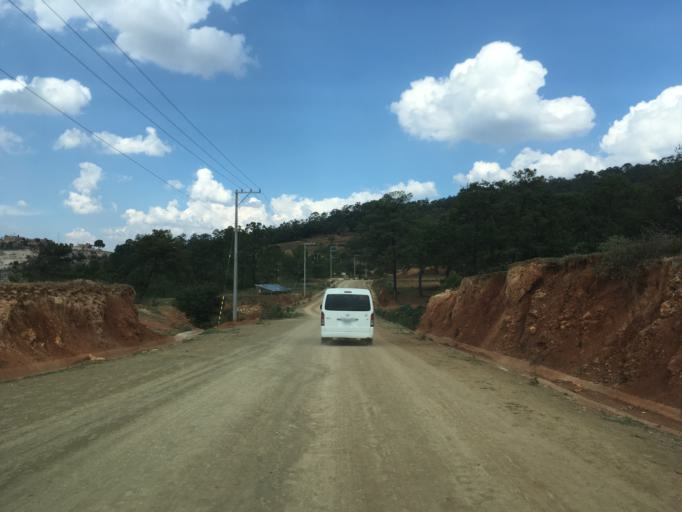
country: MX
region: Oaxaca
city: Santiago Tilantongo
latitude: 17.2179
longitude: -97.2752
